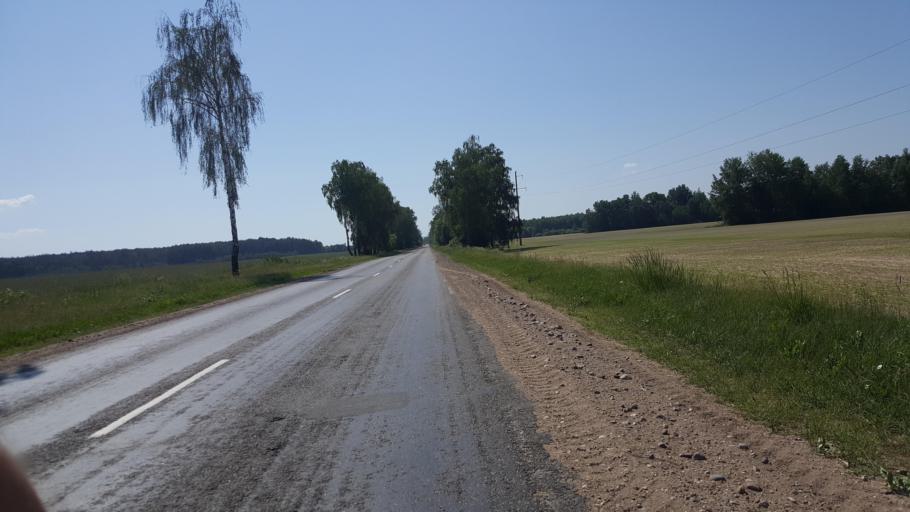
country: BY
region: Brest
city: Zhabinka
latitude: 52.2495
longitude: 23.9706
